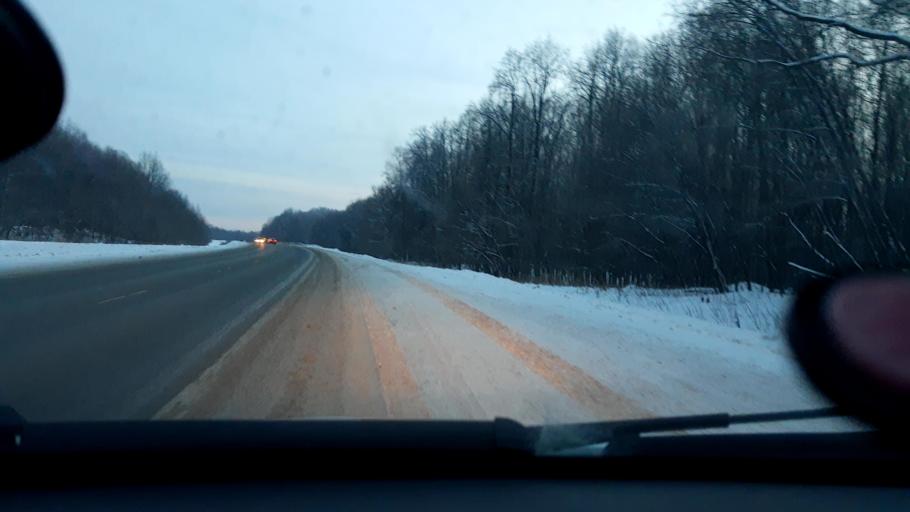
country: RU
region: Bashkortostan
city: Blagoveshchensk
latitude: 55.0098
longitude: 56.0776
